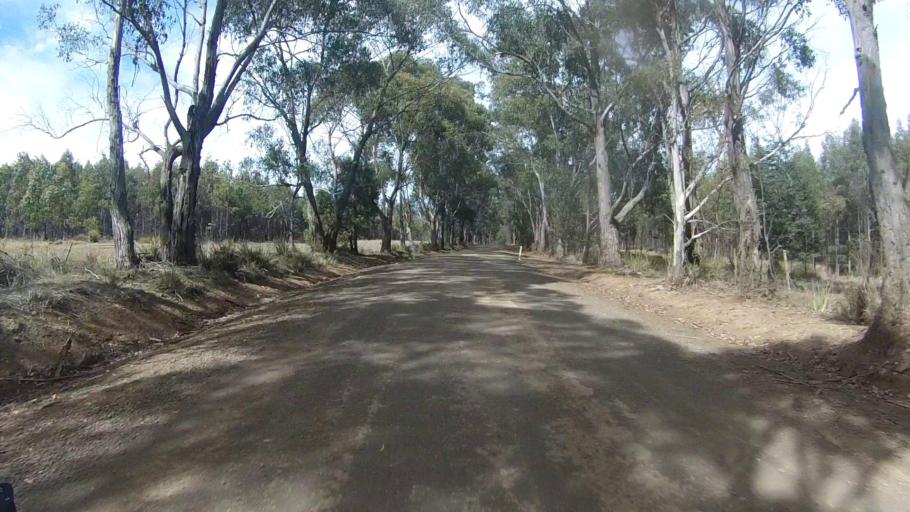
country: AU
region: Tasmania
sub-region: Sorell
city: Sorell
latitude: -42.6590
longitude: 147.8969
